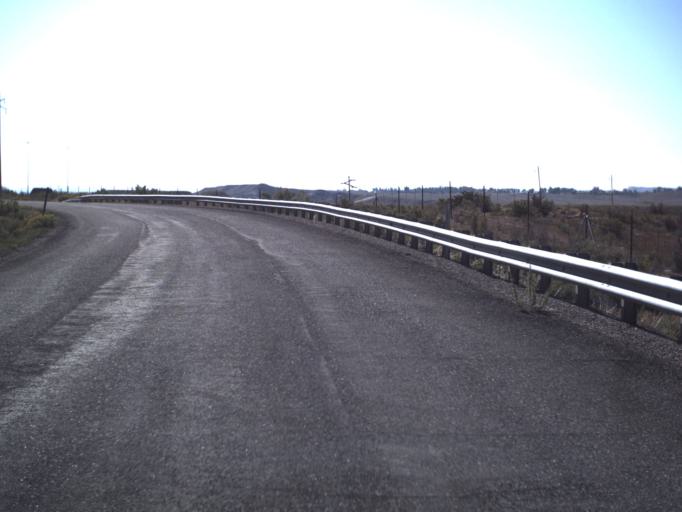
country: US
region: Utah
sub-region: Emery County
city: Castle Dale
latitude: 39.1735
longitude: -111.0492
